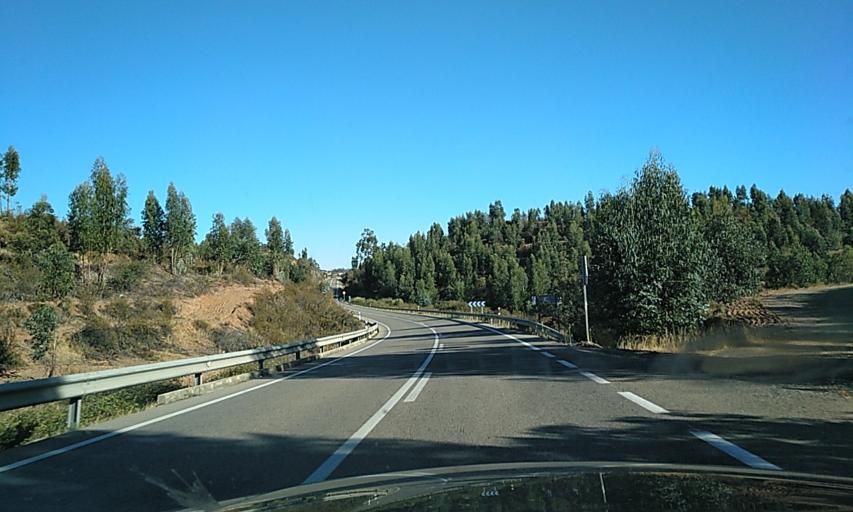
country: ES
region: Andalusia
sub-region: Provincia de Huelva
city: Santa Barbara de Casa
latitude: 37.8116
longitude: -7.2085
